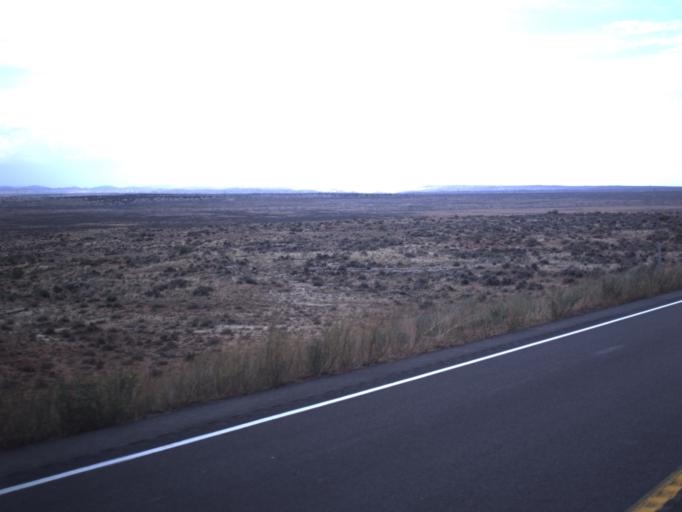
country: US
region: Utah
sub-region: Uintah County
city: Naples
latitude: 40.2546
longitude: -109.4320
